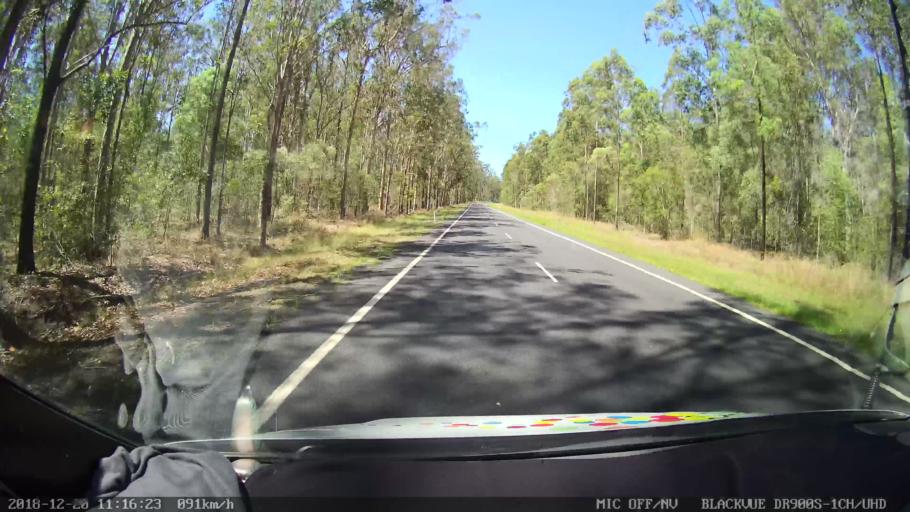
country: AU
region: New South Wales
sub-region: Richmond Valley
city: Casino
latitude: -29.0259
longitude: 153.0105
